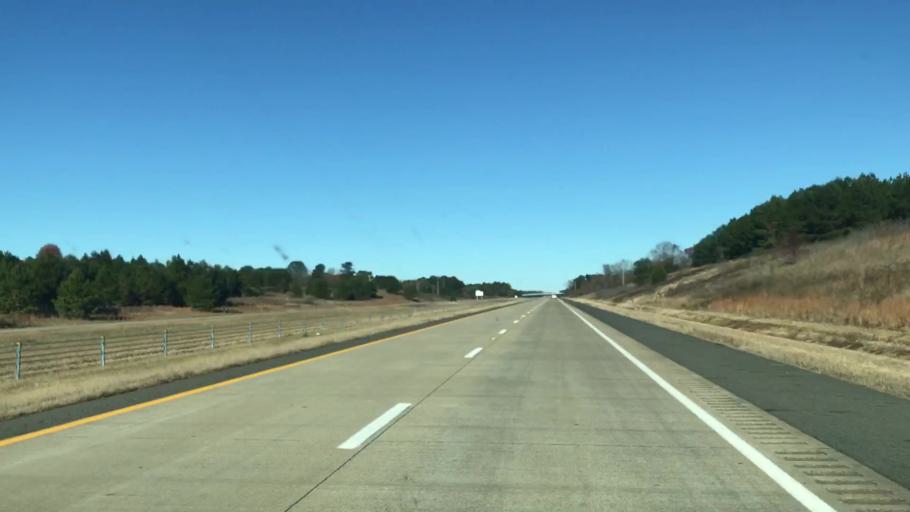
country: US
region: Texas
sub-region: Bowie County
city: Texarkana
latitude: 33.2810
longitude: -93.9092
